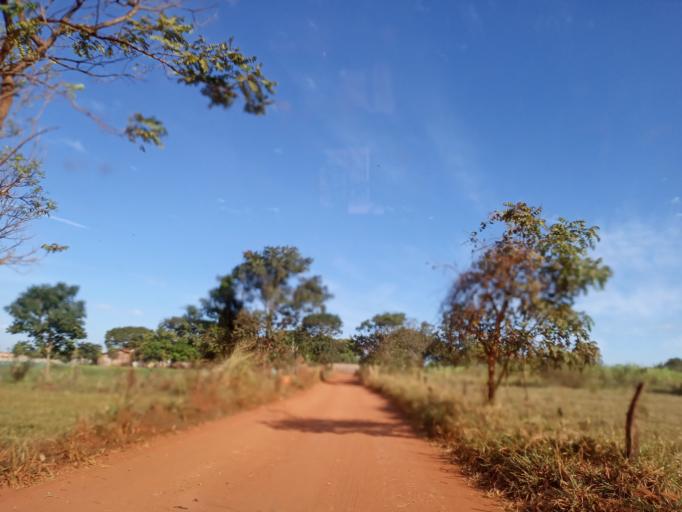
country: BR
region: Minas Gerais
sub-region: Ituiutaba
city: Ituiutaba
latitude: -18.9557
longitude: -49.4823
